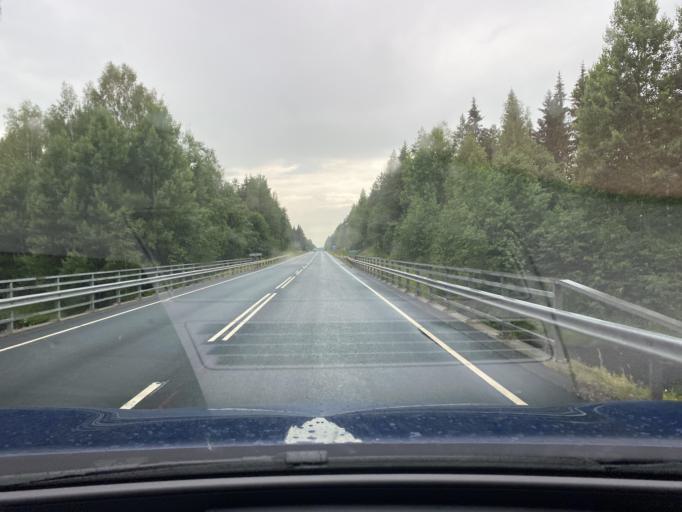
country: FI
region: Central Ostrobothnia
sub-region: Kaustinen
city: Veteli
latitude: 63.4162
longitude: 23.9453
